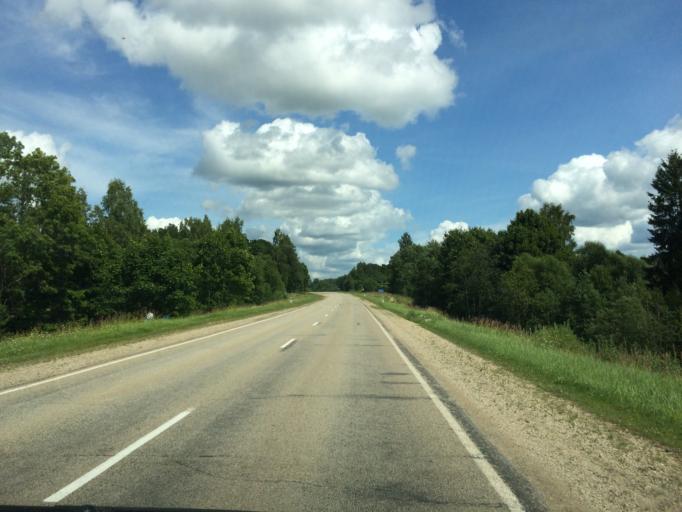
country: LV
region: Rezekne
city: Rezekne
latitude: 56.5839
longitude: 27.3956
